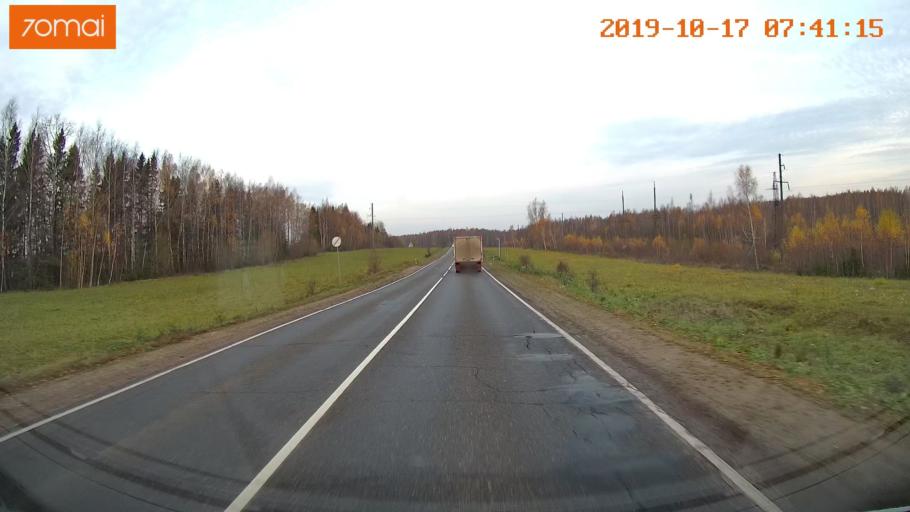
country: RU
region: Vladimir
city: Yur'yev-Pol'skiy
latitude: 56.4806
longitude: 39.8140
